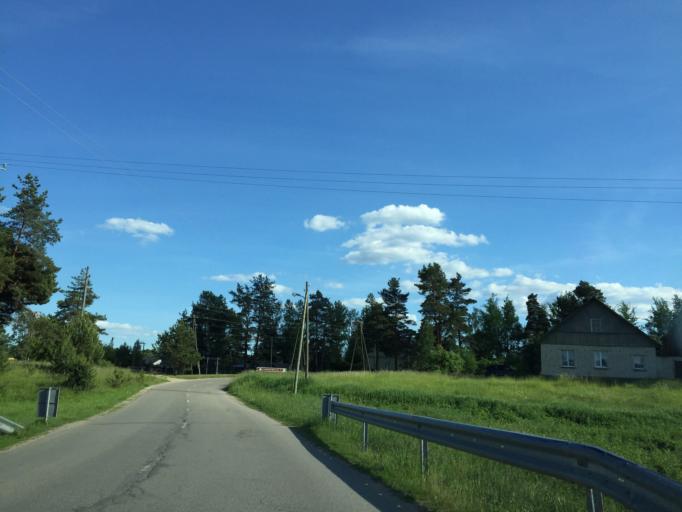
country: LV
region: Rezekne
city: Rezekne
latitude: 56.3456
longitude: 27.1668
